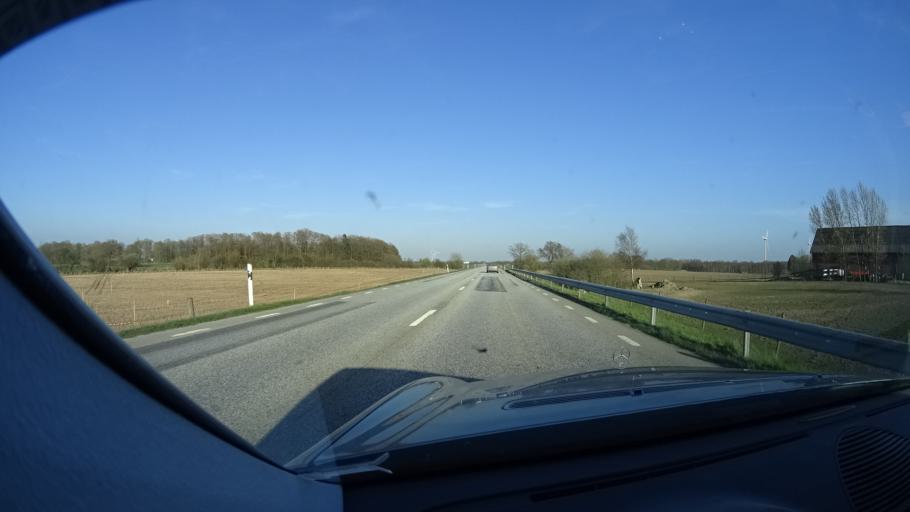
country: SE
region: Skane
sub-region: Eslovs Kommun
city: Stehag
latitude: 55.8496
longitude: 13.4250
